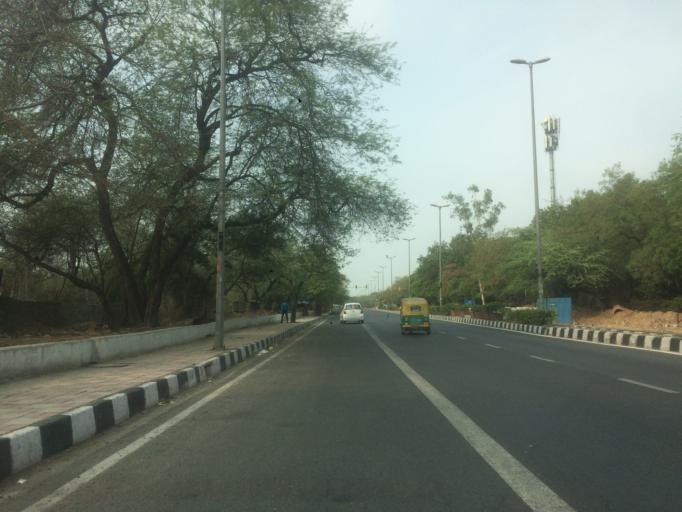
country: IN
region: NCT
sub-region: New Delhi
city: New Delhi
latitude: 28.5407
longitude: 77.1758
